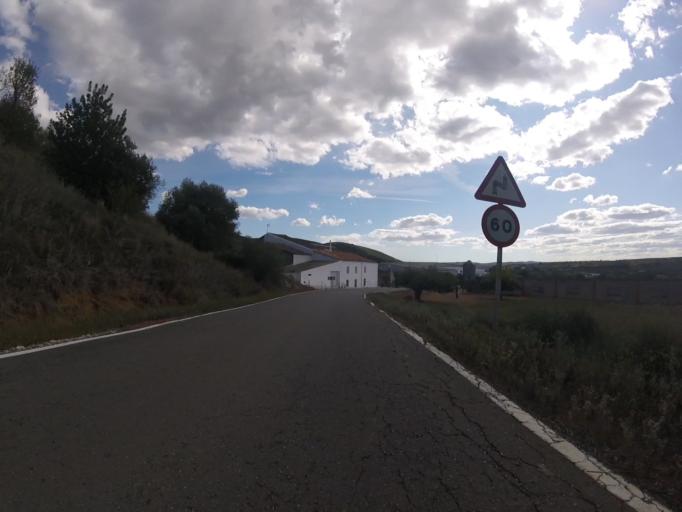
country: ES
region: Valencia
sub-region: Provincia de Castello
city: Cuevas de Vinroma
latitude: 40.3514
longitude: 0.1279
